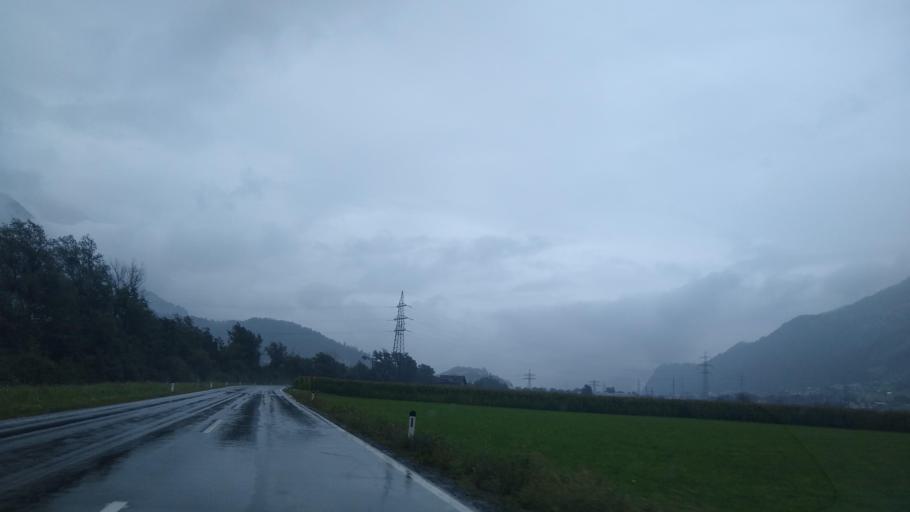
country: AT
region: Tyrol
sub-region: Politischer Bezirk Schwaz
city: Buch bei Jenbach
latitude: 47.3808
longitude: 11.7565
